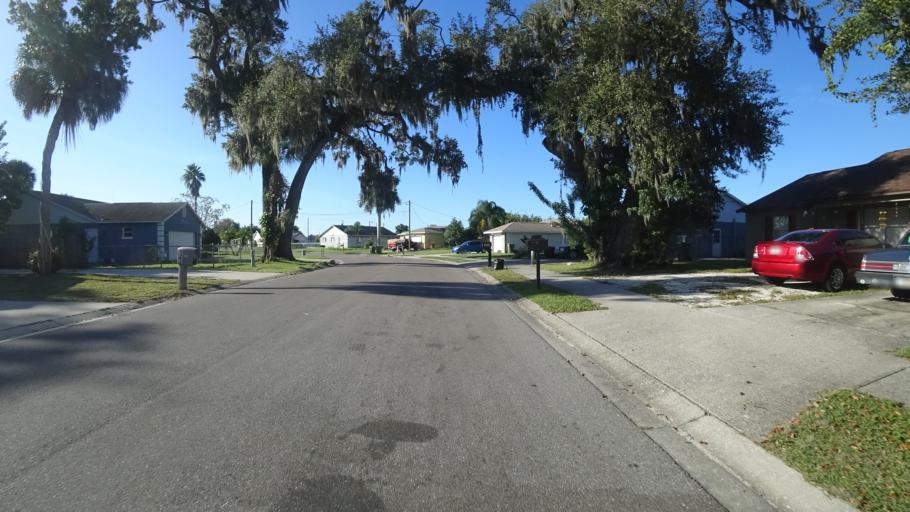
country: US
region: Florida
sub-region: Manatee County
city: Samoset
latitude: 27.4860
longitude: -82.5406
